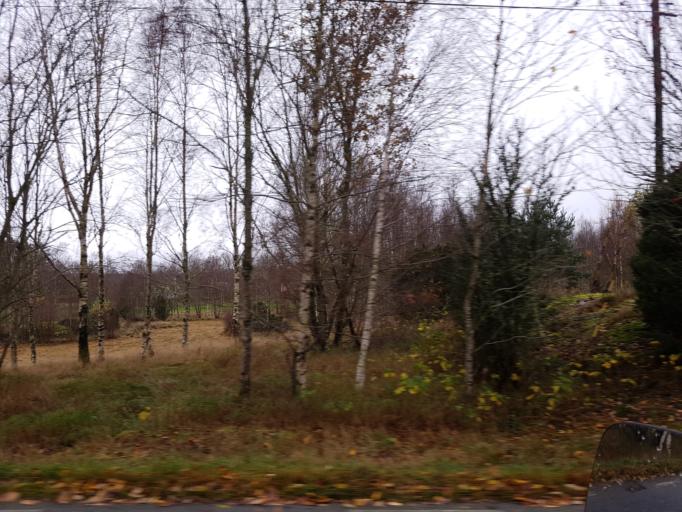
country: SE
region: Vaestra Goetaland
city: Svanesund
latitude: 58.1644
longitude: 11.7896
